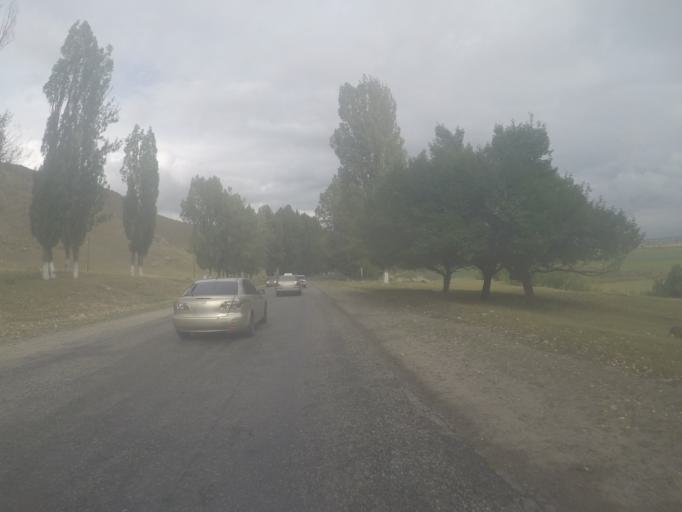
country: KG
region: Ysyk-Koel
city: Tyup
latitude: 42.7439
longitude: 78.0486
